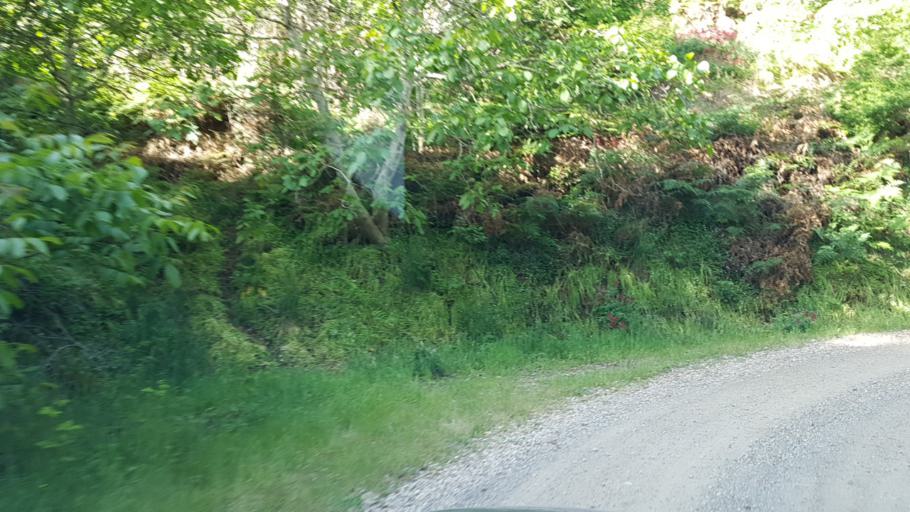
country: AU
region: South Australia
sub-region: Adelaide Hills
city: Adelaide Hills
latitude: -34.9114
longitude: 138.7604
